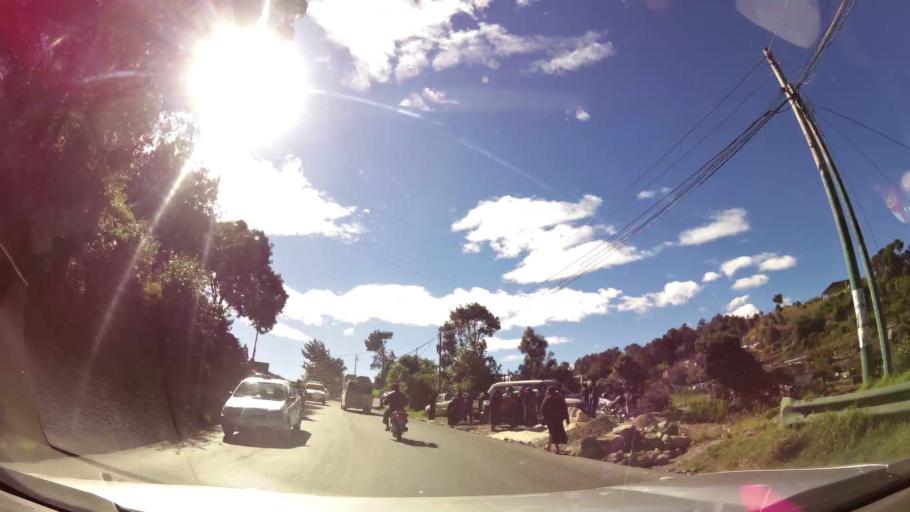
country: GT
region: Solola
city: Solola
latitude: 14.7821
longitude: -91.1807
